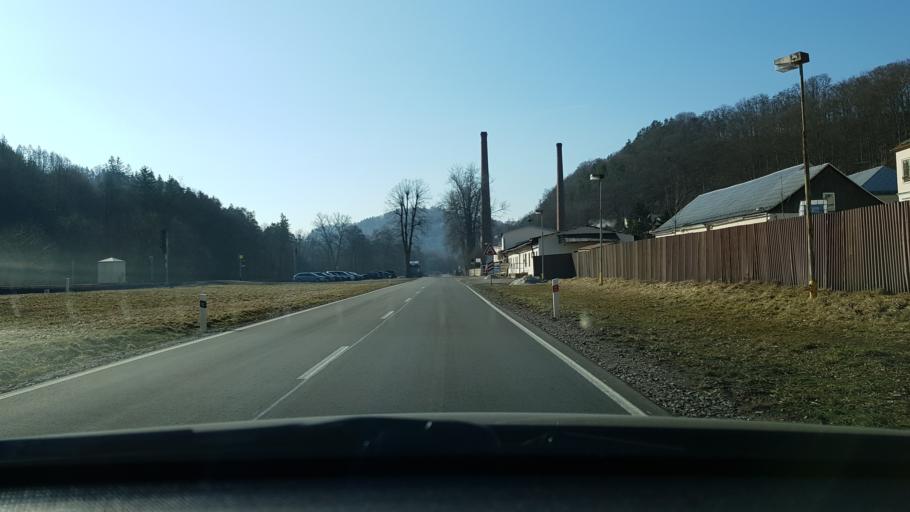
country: CZ
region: Olomoucky
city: Ruda nad Moravou
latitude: 49.9924
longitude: 16.8925
